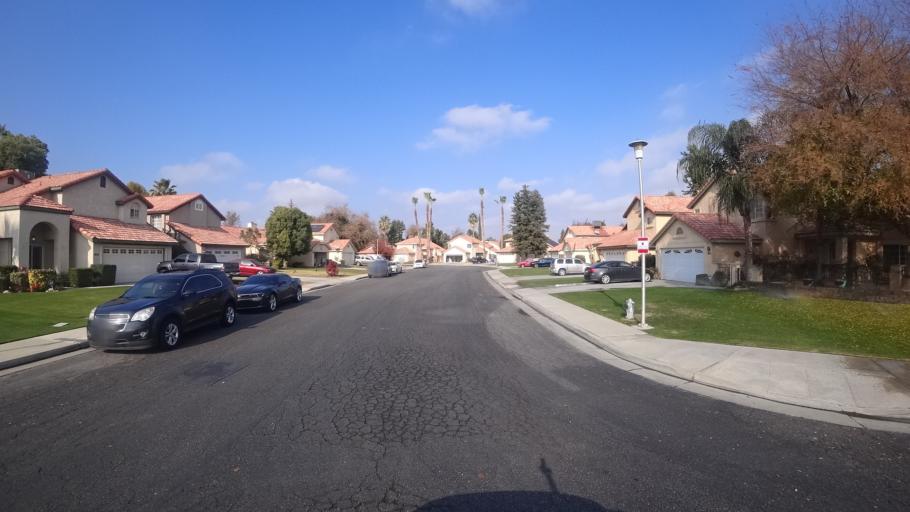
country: US
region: California
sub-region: Kern County
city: Greenacres
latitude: 35.3006
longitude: -119.0891
